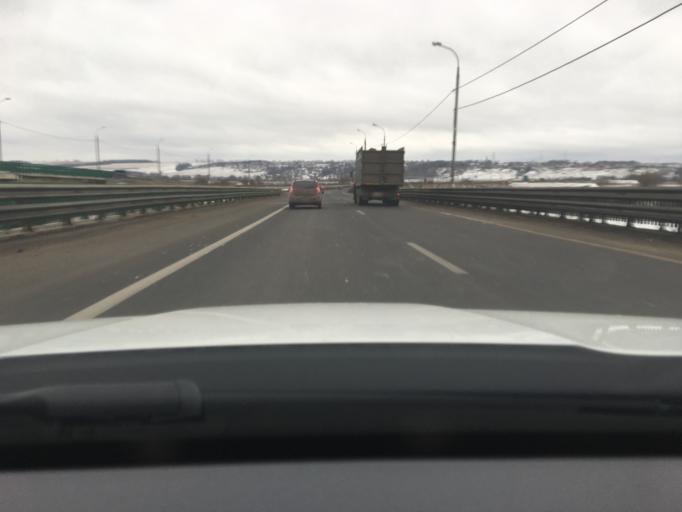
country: RU
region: Moskovskaya
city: Danki
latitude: 54.8682
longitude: 37.5027
